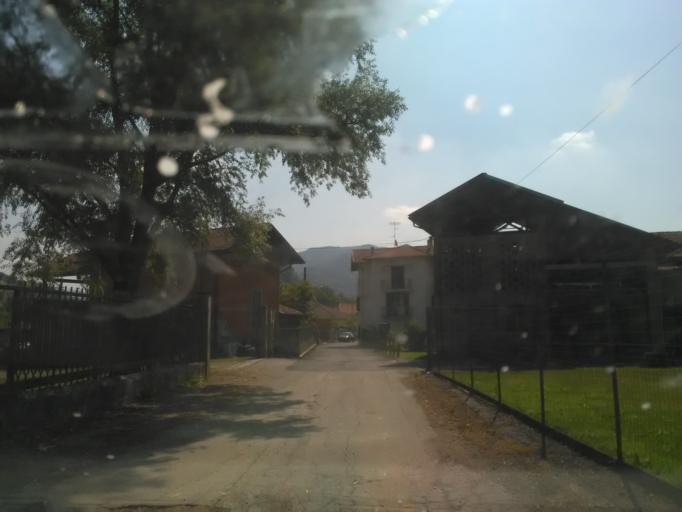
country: IT
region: Piedmont
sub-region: Provincia di Biella
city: Crevacuore
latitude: 45.6829
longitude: 8.2351
